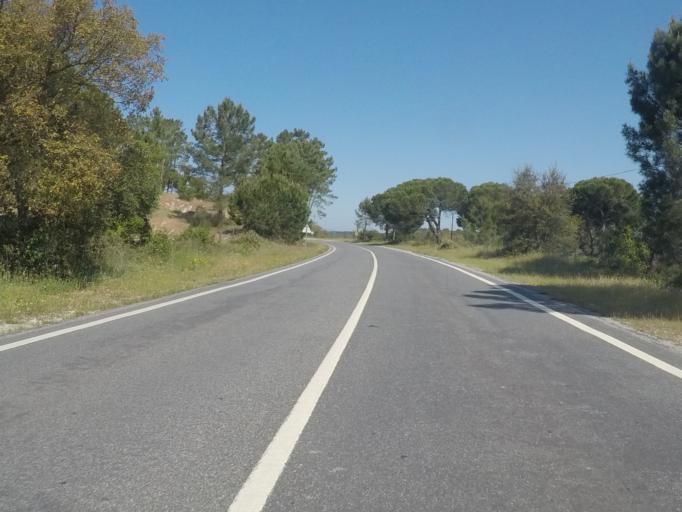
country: PT
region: Setubal
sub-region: Grandola
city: Grandola
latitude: 38.2982
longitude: -8.7256
